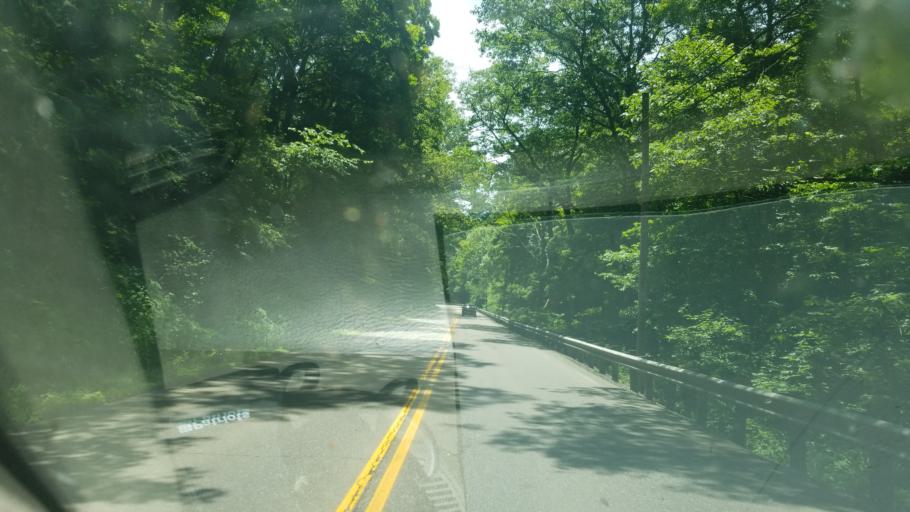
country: US
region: Ohio
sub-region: Columbiana County
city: Glenmoor
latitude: 40.7463
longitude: -80.6400
